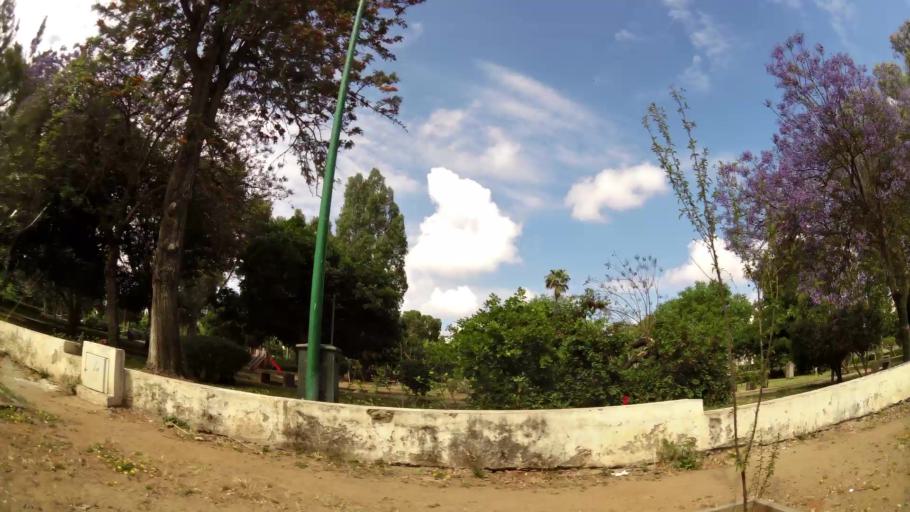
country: MA
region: Gharb-Chrarda-Beni Hssen
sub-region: Kenitra Province
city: Kenitra
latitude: 34.2577
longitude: -6.5787
